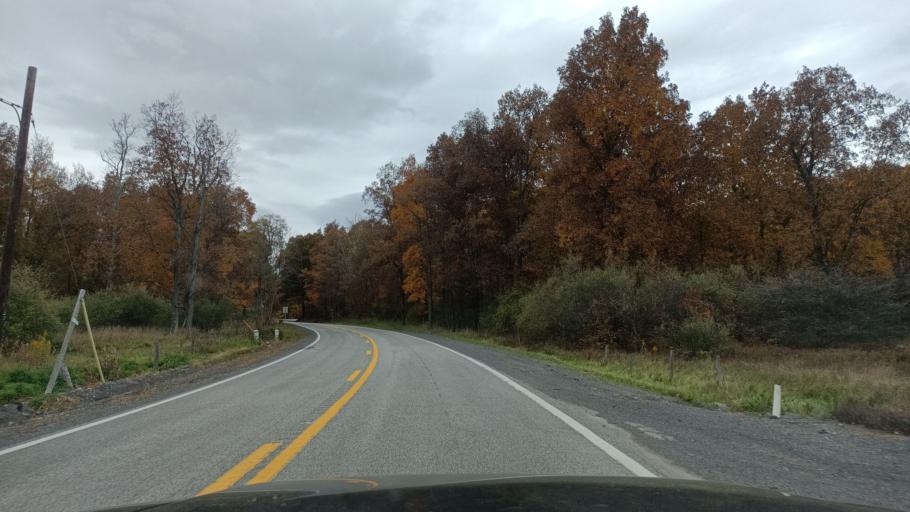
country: US
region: Maryland
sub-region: Garrett County
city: Mountain Lake Park
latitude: 39.2438
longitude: -79.2232
